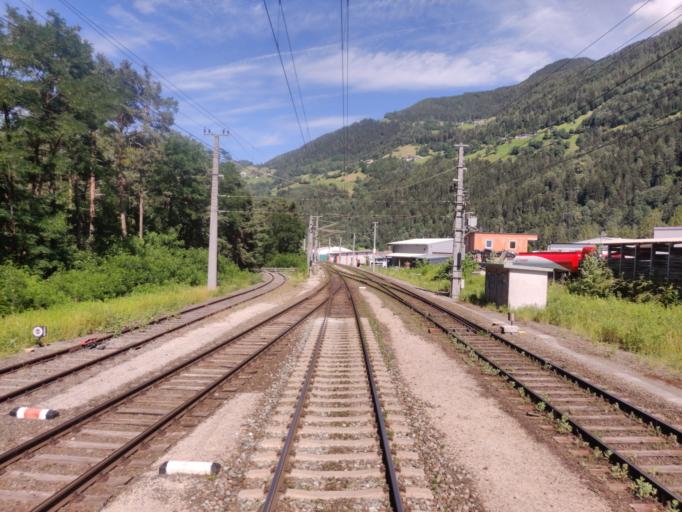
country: AT
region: Tyrol
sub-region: Politischer Bezirk Imst
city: Haiming
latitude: 47.2393
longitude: 10.8675
